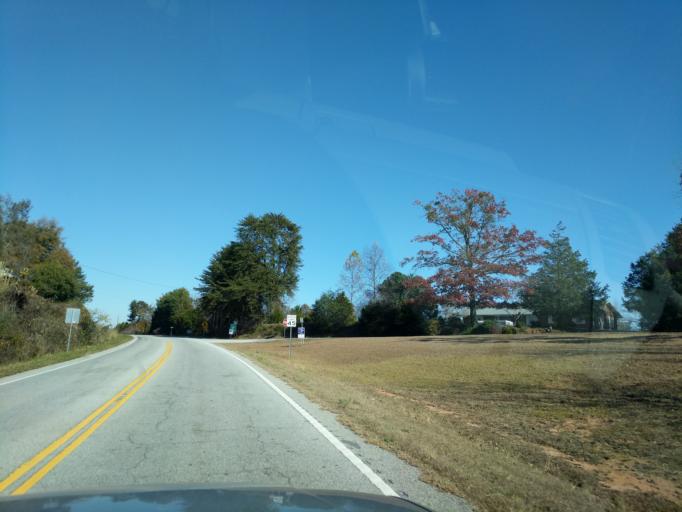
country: US
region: South Carolina
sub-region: Spartanburg County
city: Landrum
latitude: 35.1633
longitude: -82.1993
